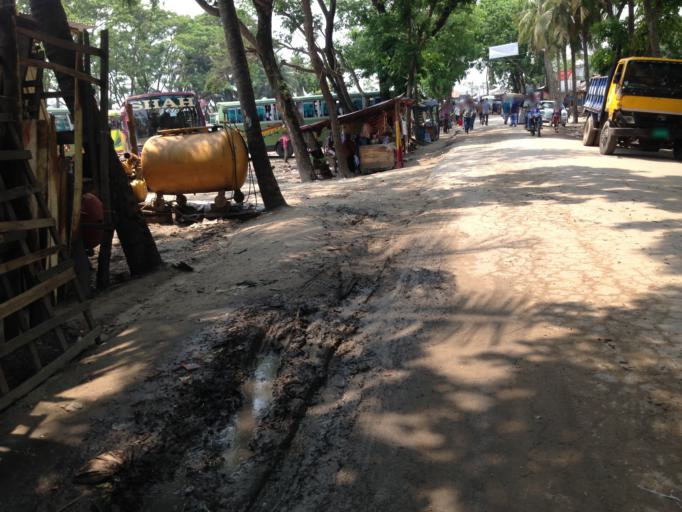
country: BD
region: Chittagong
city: Lakshmipur
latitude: 22.8745
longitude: 90.7856
